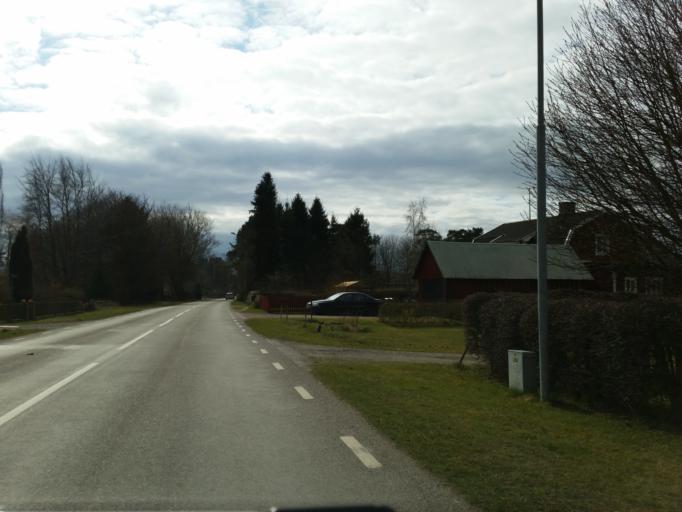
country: SE
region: Kalmar
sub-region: Morbylanga Kommun
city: Sodra Sandby
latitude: 56.6442
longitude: 16.6725
